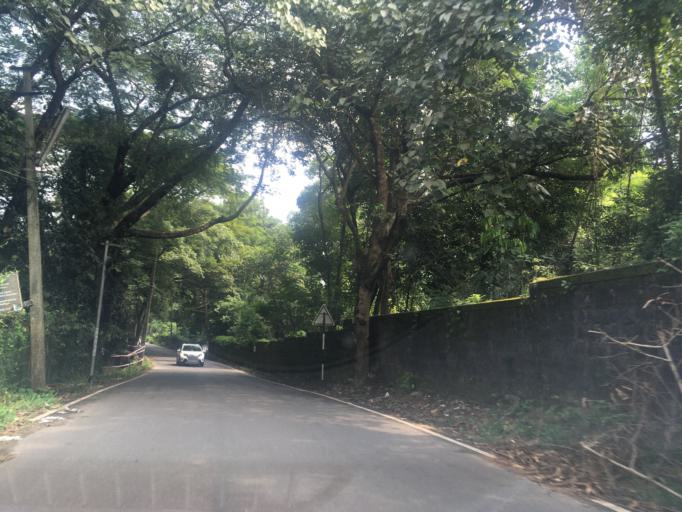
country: IN
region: Kerala
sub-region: Ernakulam
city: Elur
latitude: 10.0448
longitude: 76.3063
